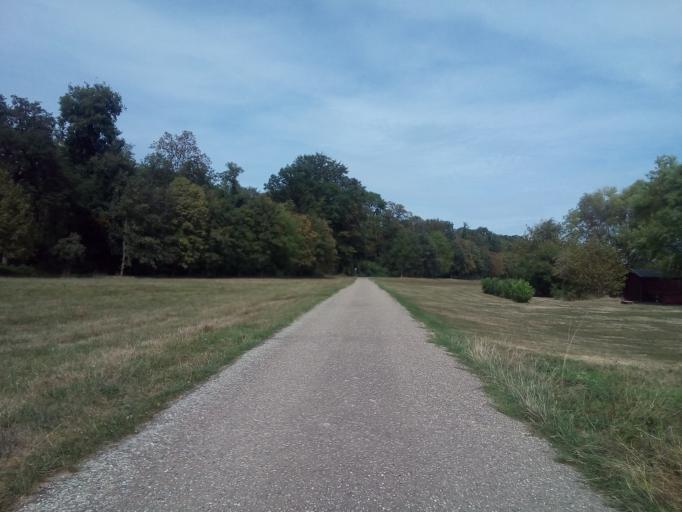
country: DE
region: Baden-Wuerttemberg
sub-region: Karlsruhe Region
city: Zell
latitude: 48.7084
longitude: 8.0565
